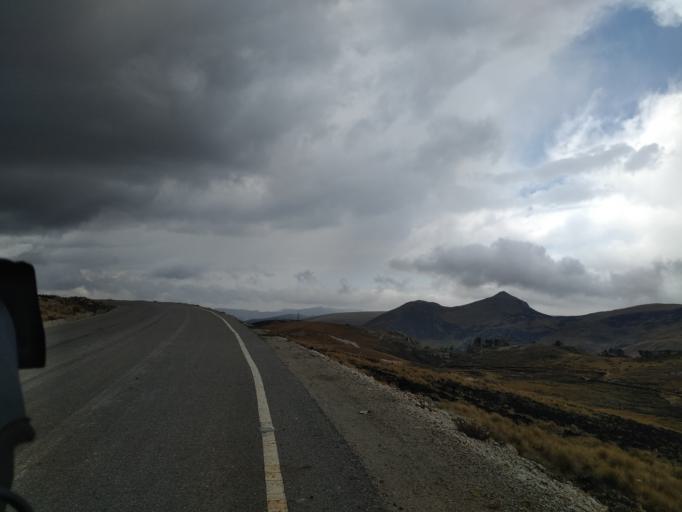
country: PE
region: La Libertad
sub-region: Provincia de Santiago de Chuco
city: Quiruvilca
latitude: -7.9929
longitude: -78.2975
